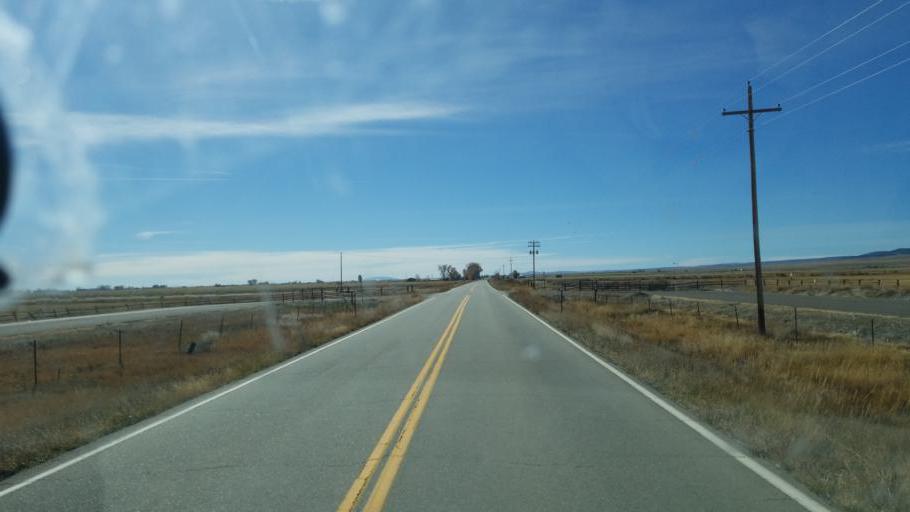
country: US
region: Colorado
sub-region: Rio Grande County
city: Monte Vista
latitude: 37.4674
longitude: -106.1486
